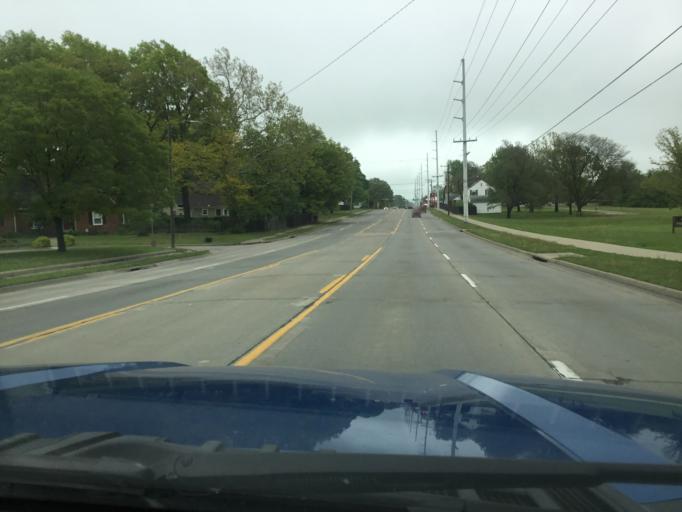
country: US
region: Kansas
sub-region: Shawnee County
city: Topeka
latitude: 39.0296
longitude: -95.7148
